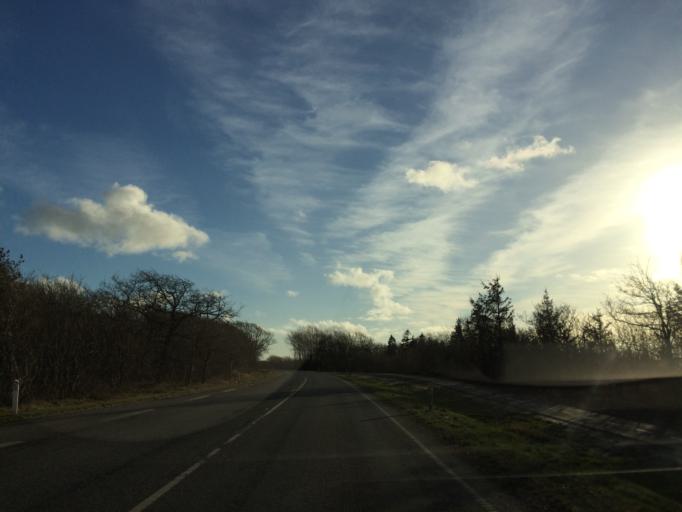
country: DK
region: Central Jutland
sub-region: Holstebro Kommune
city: Ulfborg
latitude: 56.3157
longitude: 8.3390
